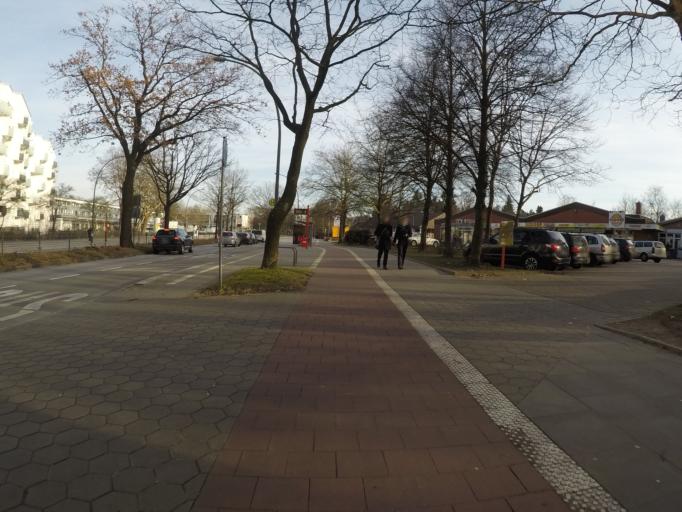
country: DE
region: Schleswig-Holstein
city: Halstenbek
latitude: 53.5842
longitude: 9.8524
